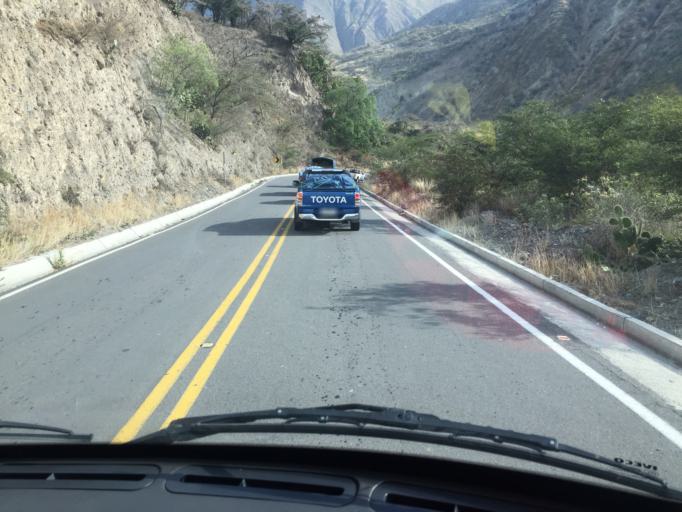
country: EC
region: Carchi
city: El Angel
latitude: 0.6043
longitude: -78.1370
